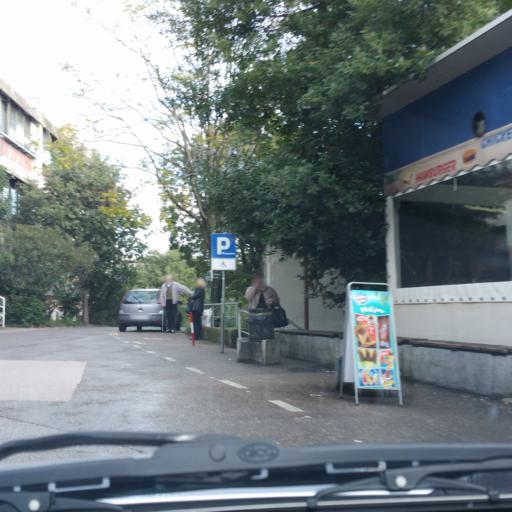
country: HR
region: Primorsko-Goranska
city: Drenova
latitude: 45.3327
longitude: 14.4271
